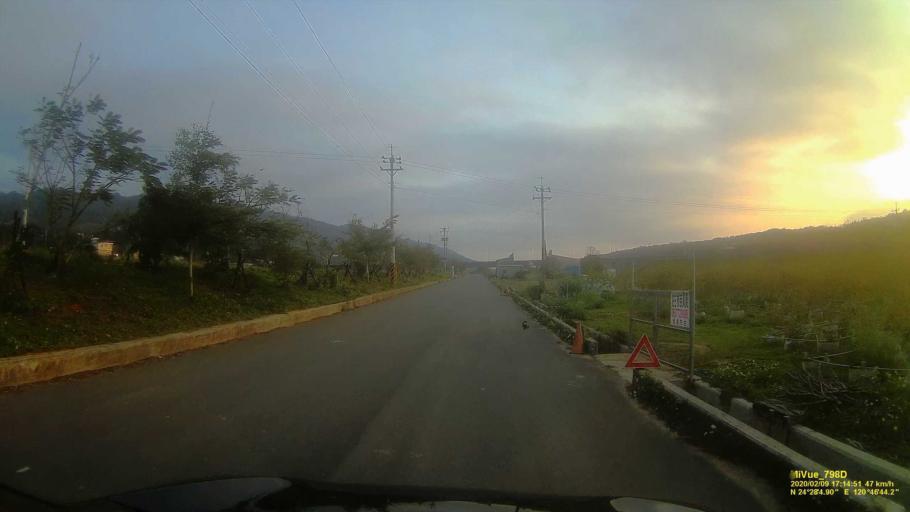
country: TW
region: Taiwan
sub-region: Miaoli
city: Miaoli
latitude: 24.4677
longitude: 120.7789
